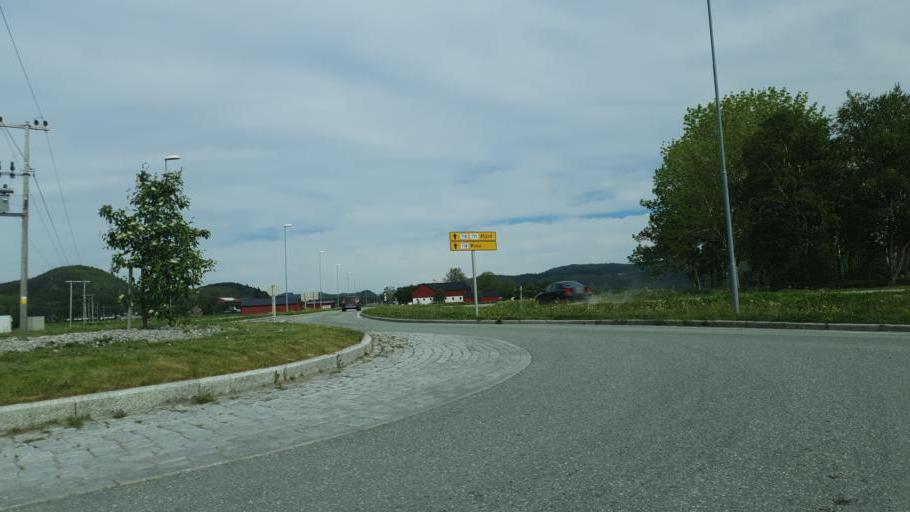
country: NO
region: Sor-Trondelag
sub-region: Rissa
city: Rissa
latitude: 63.5802
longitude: 9.9361
